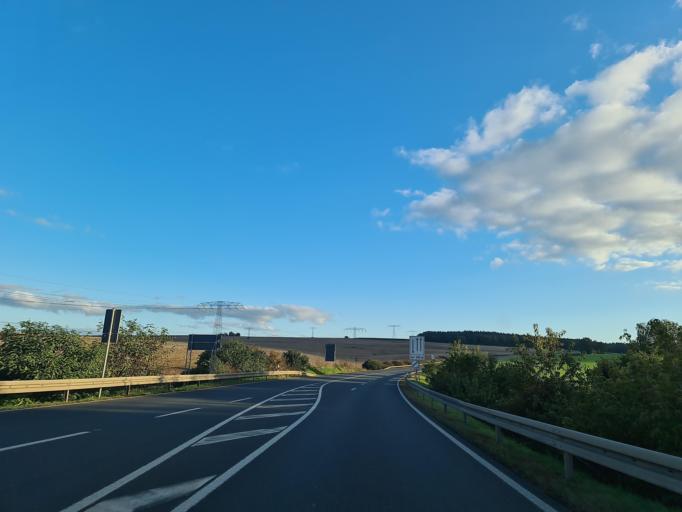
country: DE
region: Thuringia
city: Teichwitz
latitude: 50.7664
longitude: 12.0884
